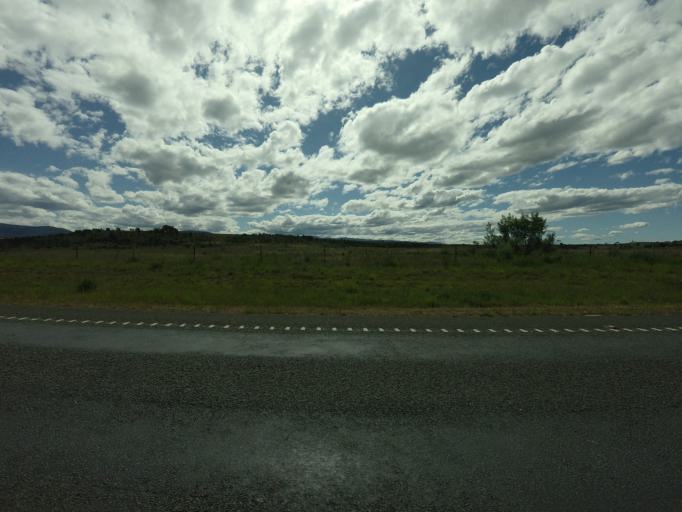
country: AU
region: Tasmania
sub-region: Northern Midlands
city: Evandale
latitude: -42.1368
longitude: 147.4228
